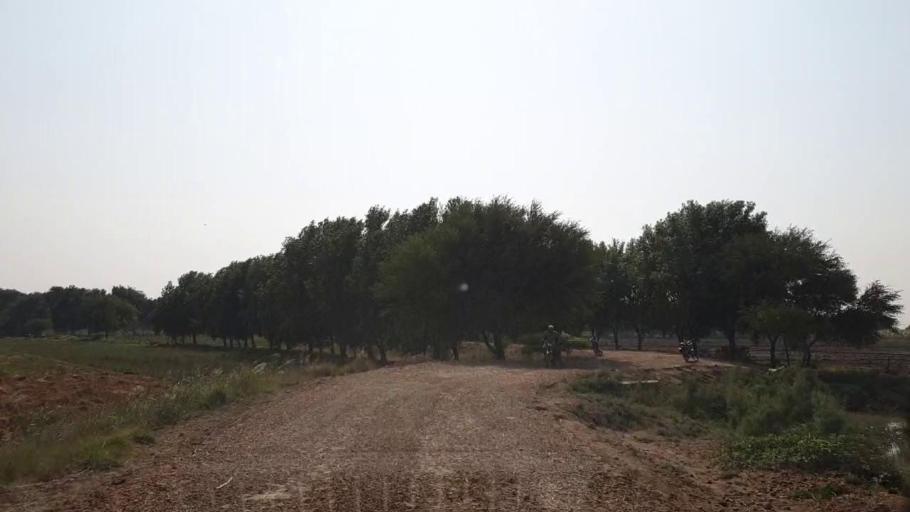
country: PK
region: Sindh
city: Tando Muhammad Khan
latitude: 25.0172
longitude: 68.4178
